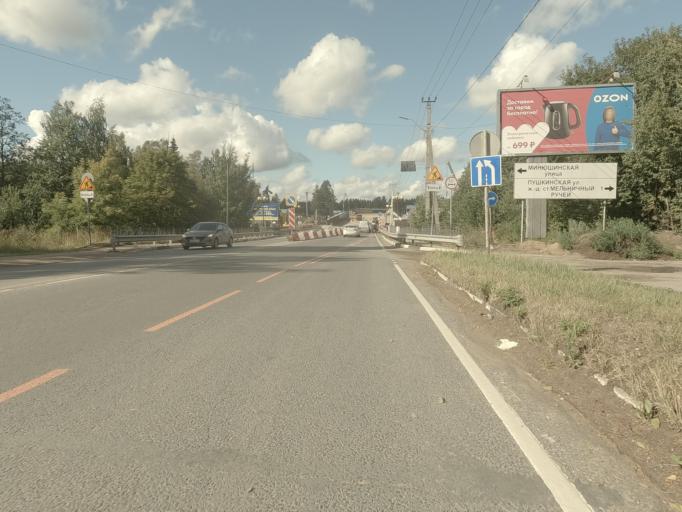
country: RU
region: Leningrad
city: Vsevolozhsk
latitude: 60.0125
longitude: 30.6663
